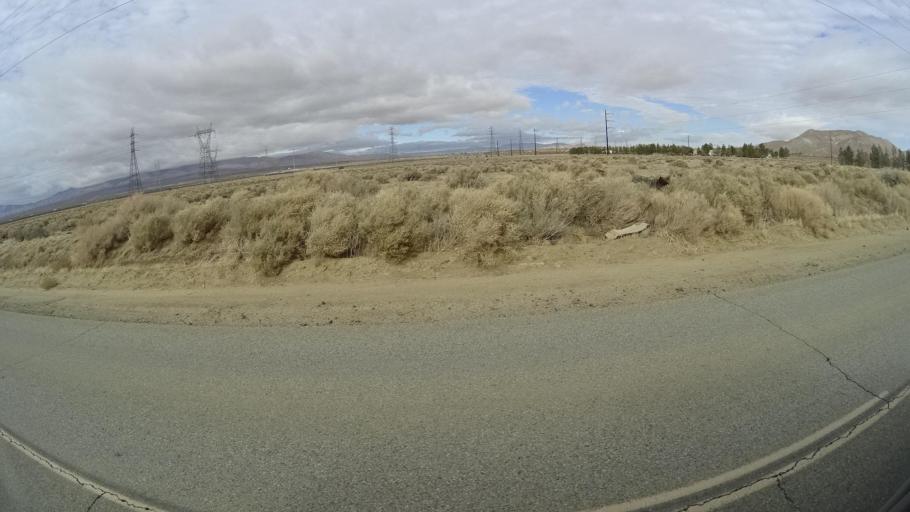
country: US
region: California
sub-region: Kern County
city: Rosamond
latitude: 34.8633
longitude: -118.3102
